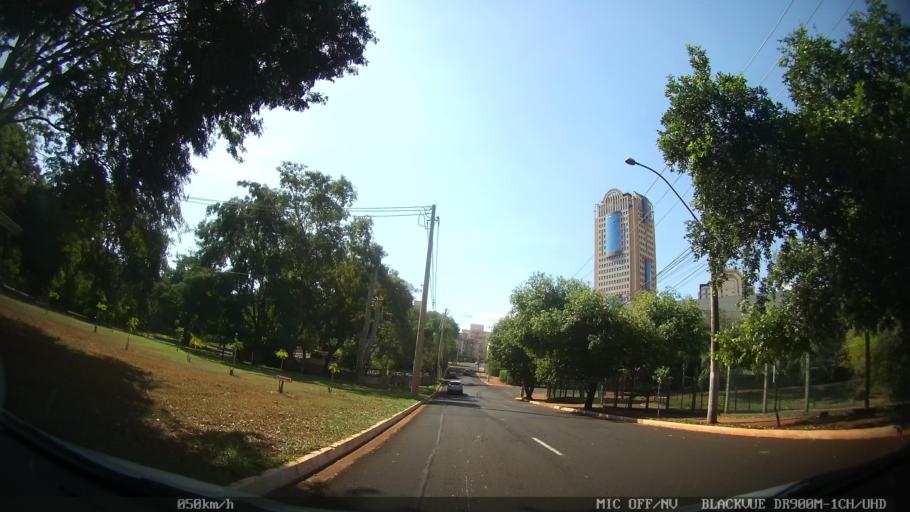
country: BR
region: Sao Paulo
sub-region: Ribeirao Preto
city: Ribeirao Preto
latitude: -21.2133
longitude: -47.8199
